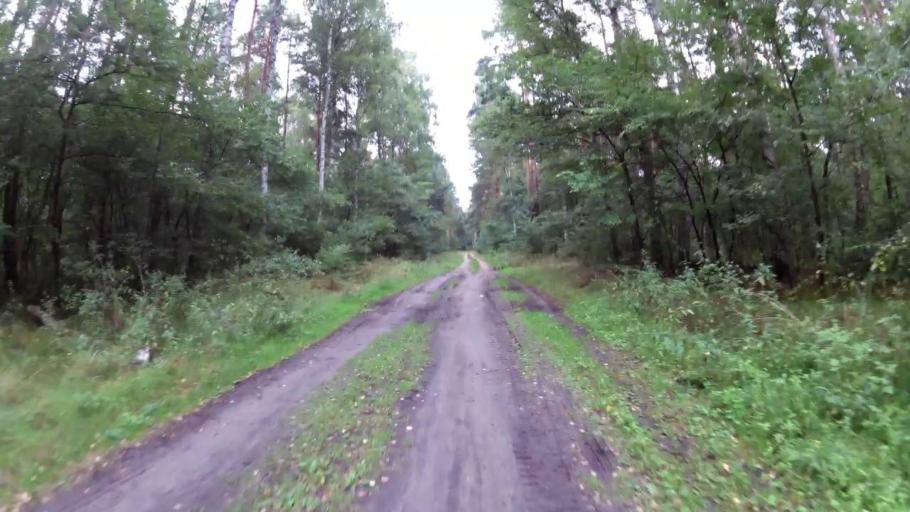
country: PL
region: West Pomeranian Voivodeship
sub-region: Powiat mysliborski
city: Debno
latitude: 52.7843
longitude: 14.7161
